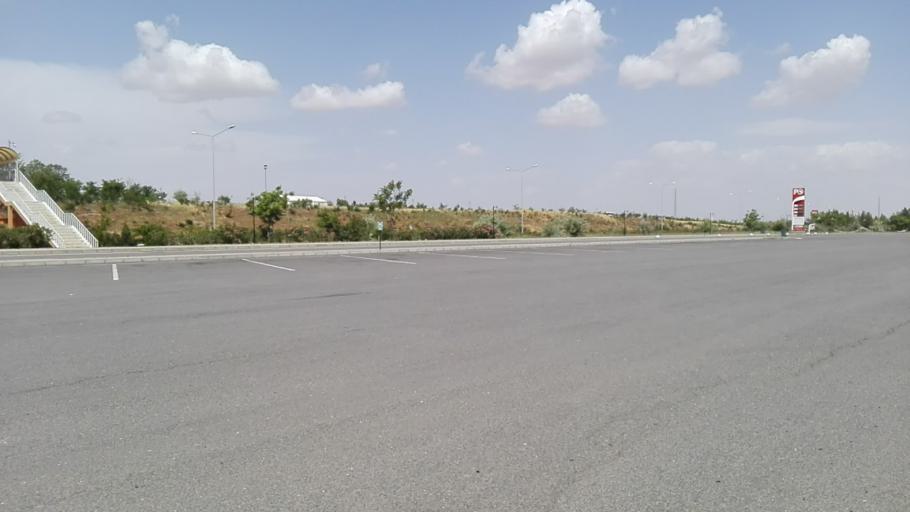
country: TR
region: Sanliurfa
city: Bogurtlen
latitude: 37.0987
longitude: 38.1888
